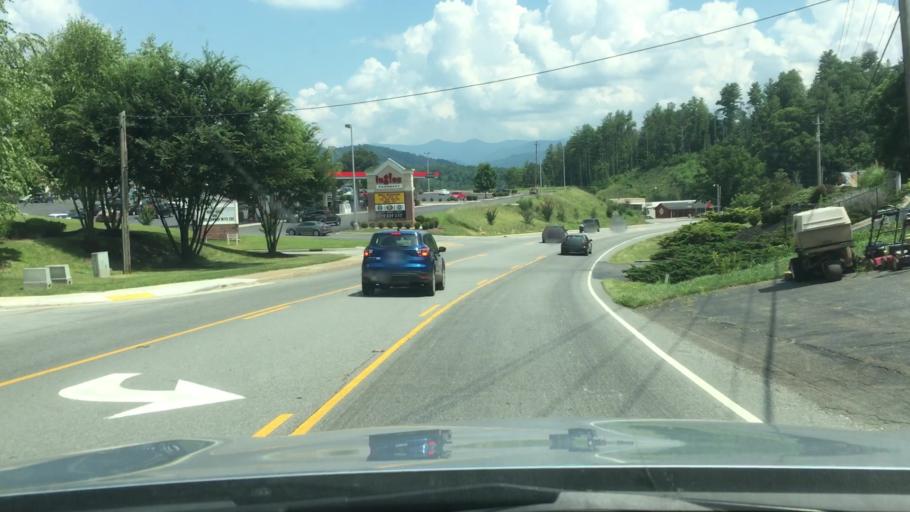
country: US
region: North Carolina
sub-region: Madison County
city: Mars Hill
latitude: 35.8250
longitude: -82.5460
